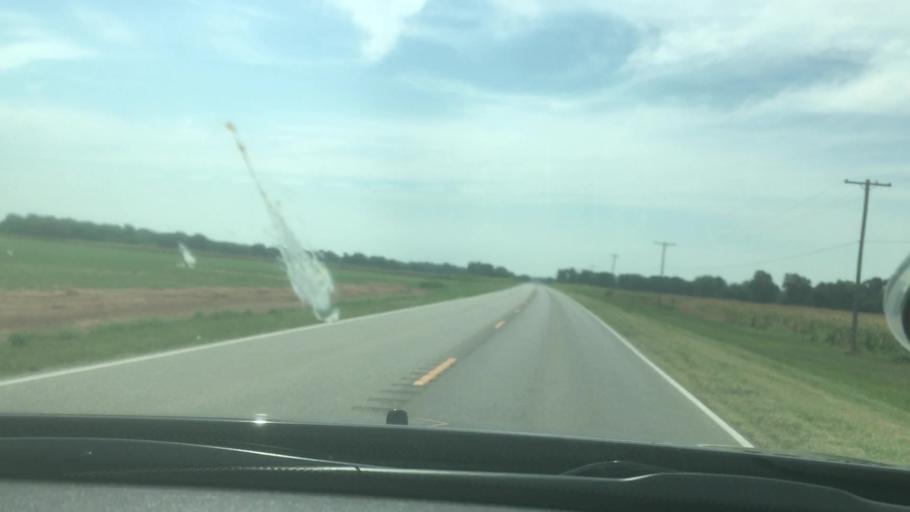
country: US
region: Oklahoma
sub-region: Garvin County
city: Maysville
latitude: 34.7949
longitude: -97.3534
